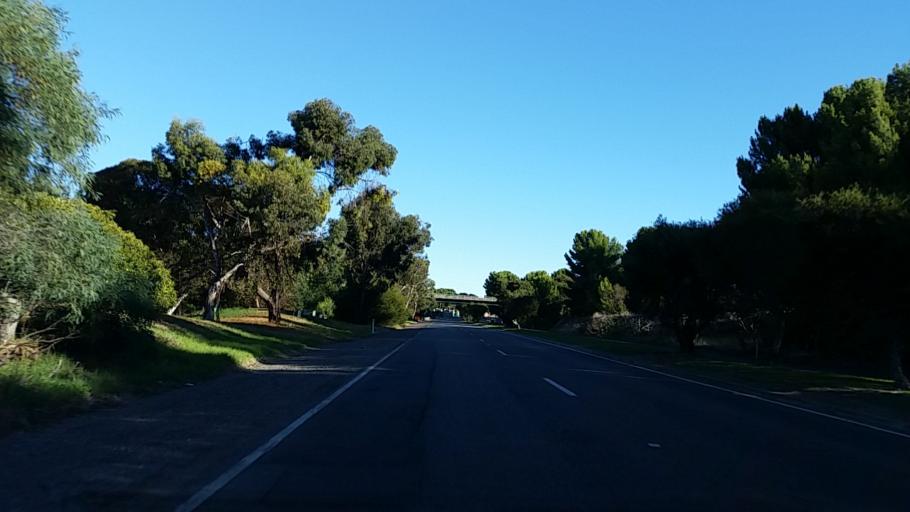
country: AU
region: South Australia
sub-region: Onkaparinga
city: Reynella
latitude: -35.0919
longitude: 138.5372
